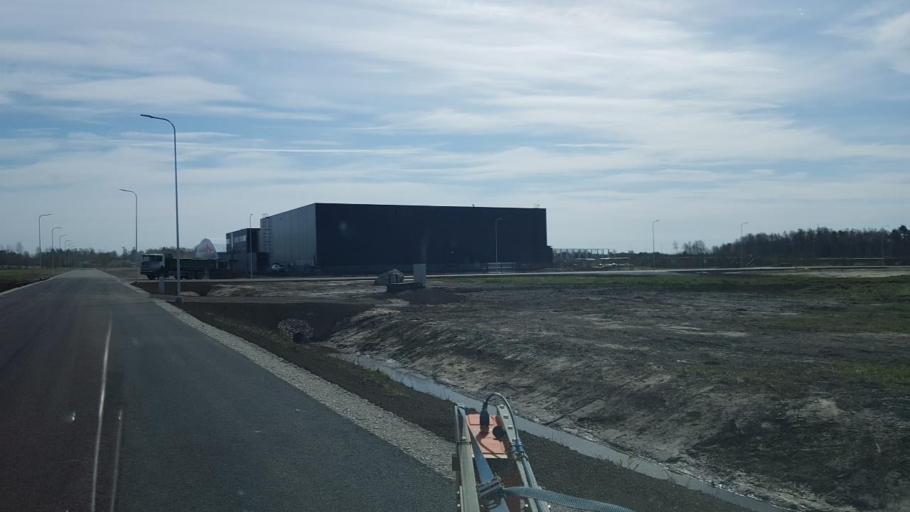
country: EE
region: Harju
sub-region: Kiili vald
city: Kiili
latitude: 59.3360
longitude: 24.7946
